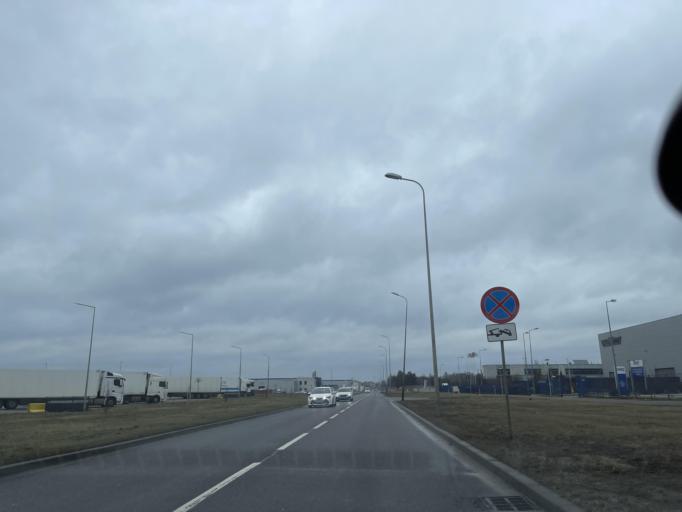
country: PL
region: Kujawsko-Pomorskie
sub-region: Bydgoszcz
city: Bydgoszcz
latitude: 53.0802
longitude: 18.0757
